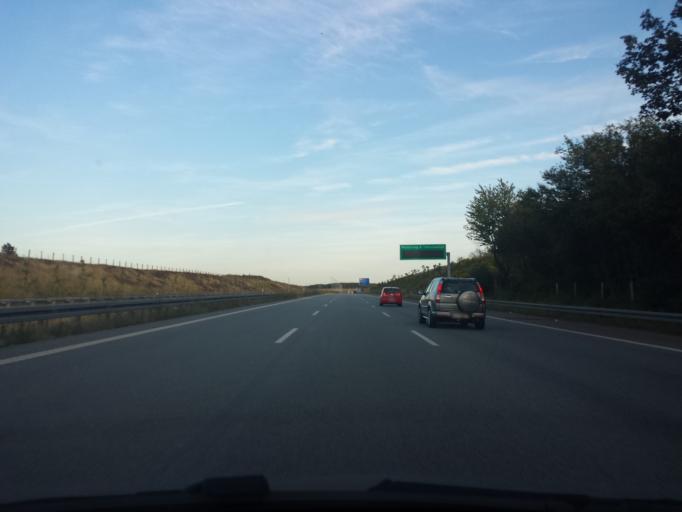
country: DK
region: Capital Region
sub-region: Glostrup Kommune
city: Glostrup
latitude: 55.6974
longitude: 12.3857
